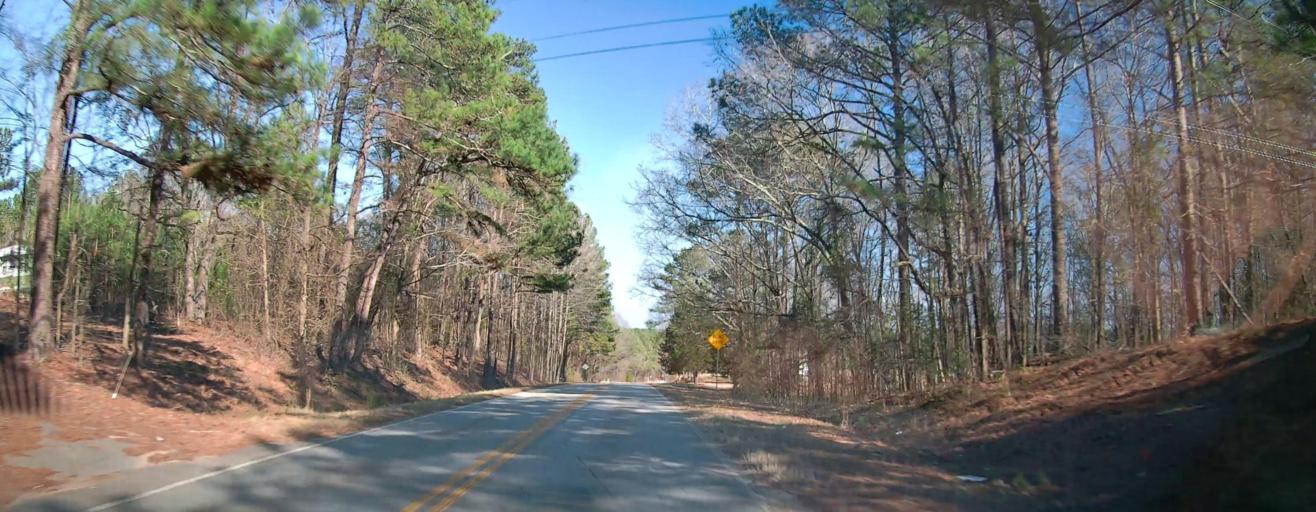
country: US
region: Georgia
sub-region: Monroe County
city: Forsyth
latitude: 33.0569
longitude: -83.8797
